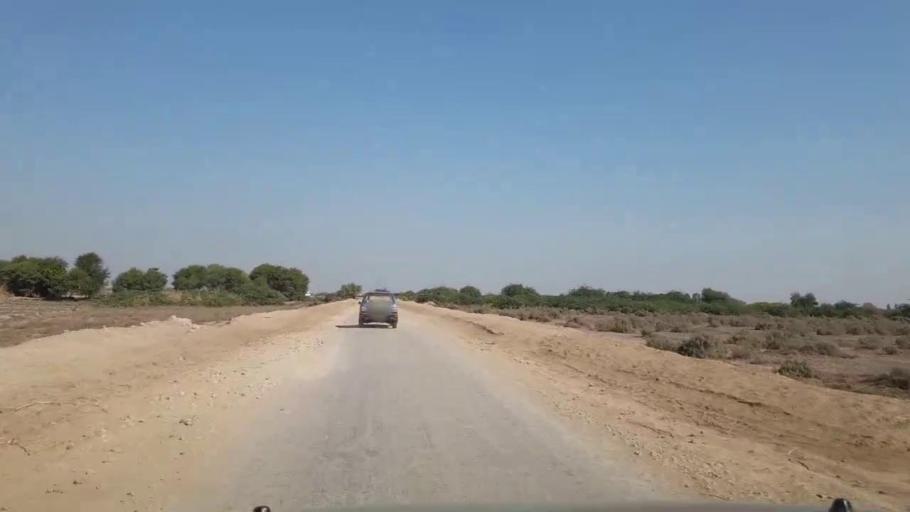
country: PK
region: Sindh
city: Digri
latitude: 24.9582
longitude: 69.1121
